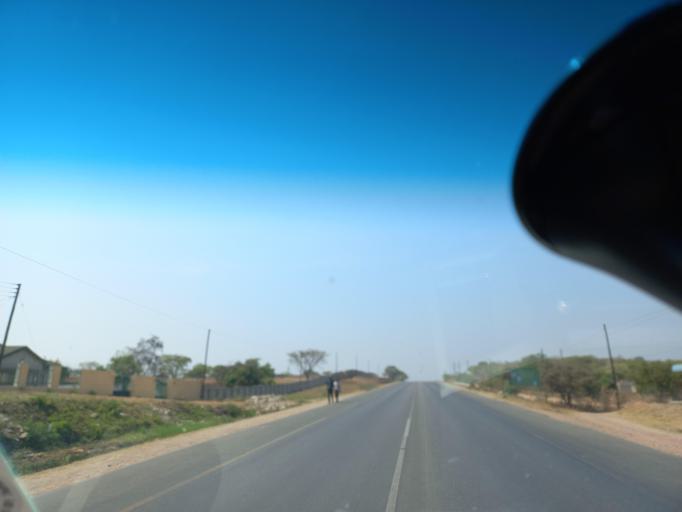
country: ZM
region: Lusaka
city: Lusaka
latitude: -15.5699
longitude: 28.2718
